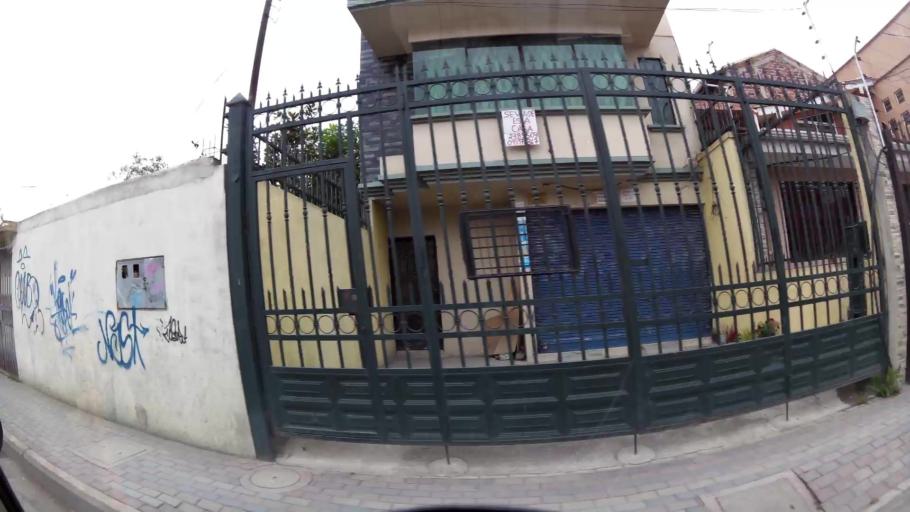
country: EC
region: Azuay
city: Cuenca
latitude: -2.9231
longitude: -79.0389
